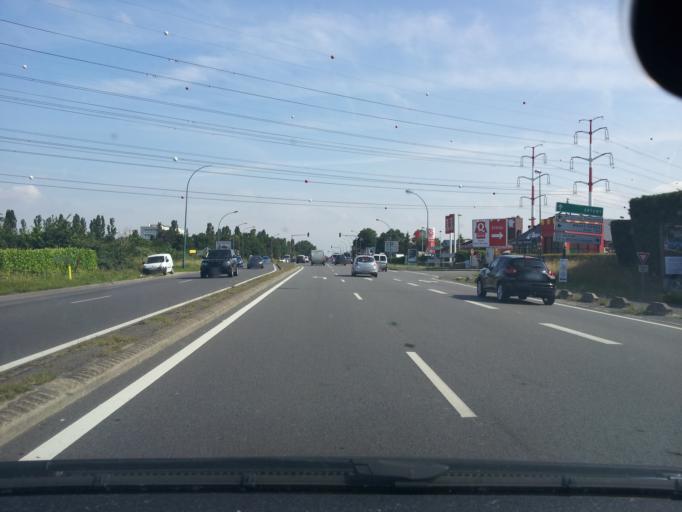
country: FR
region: Ile-de-France
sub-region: Departement de l'Essonne
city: Massy
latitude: 48.7286
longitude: 2.3004
